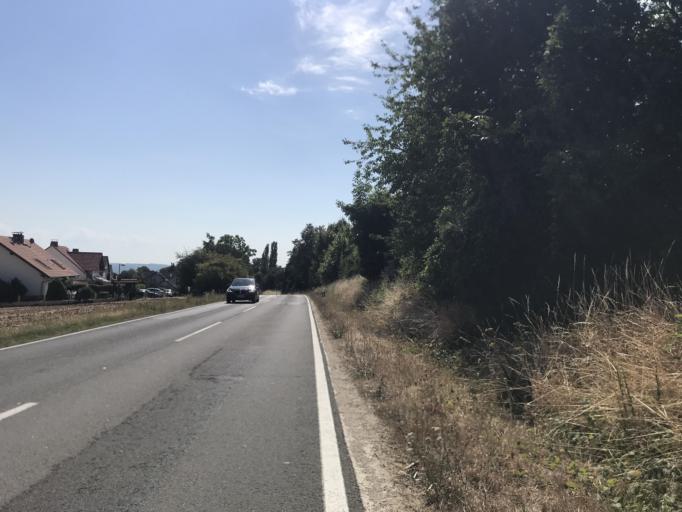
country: DE
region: Hesse
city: Geisenheim
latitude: 50.0126
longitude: 7.9709
